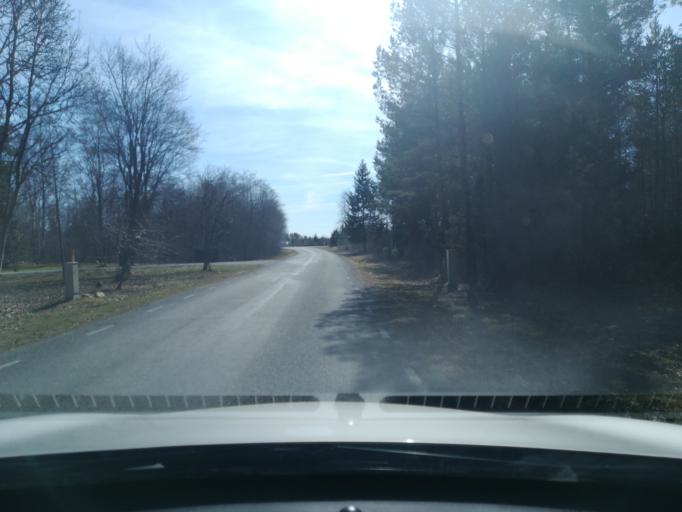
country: EE
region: Harju
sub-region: Saue linn
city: Saue
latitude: 59.3033
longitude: 24.5879
